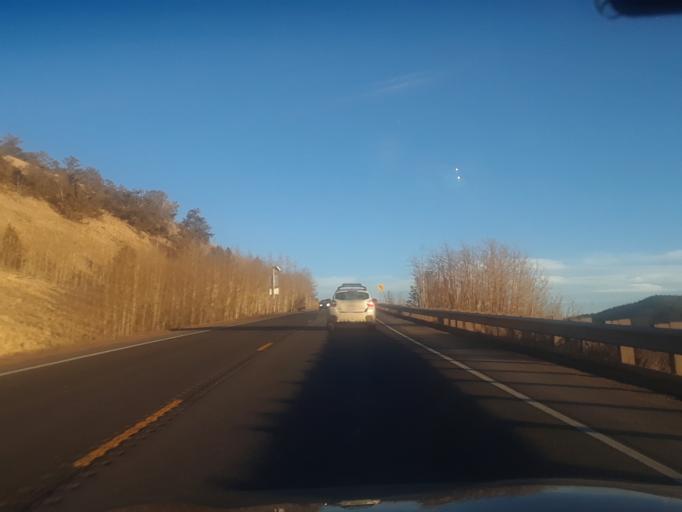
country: US
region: Colorado
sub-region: Summit County
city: Breckenridge
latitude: 39.4041
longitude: -105.7661
